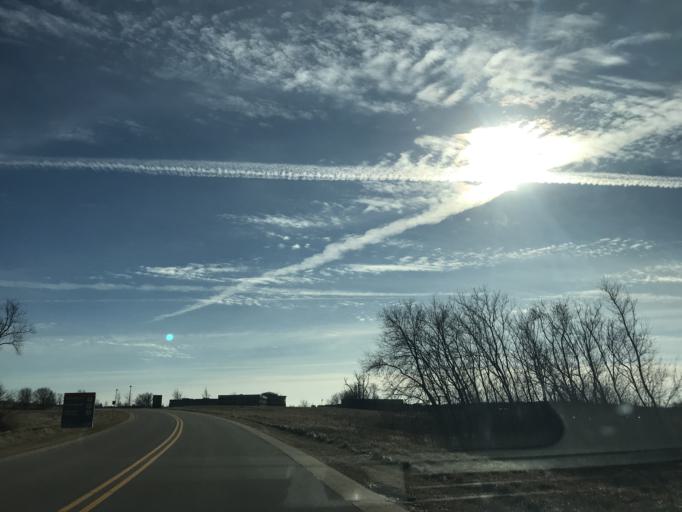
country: US
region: Wisconsin
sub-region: Dane County
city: Windsor
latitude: 43.1566
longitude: -89.2973
